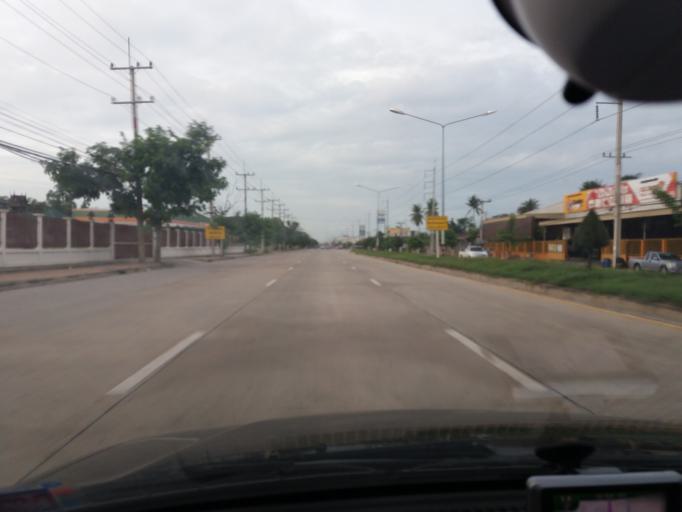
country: TH
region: Suphan Buri
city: U Thong
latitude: 14.3899
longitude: 99.8952
